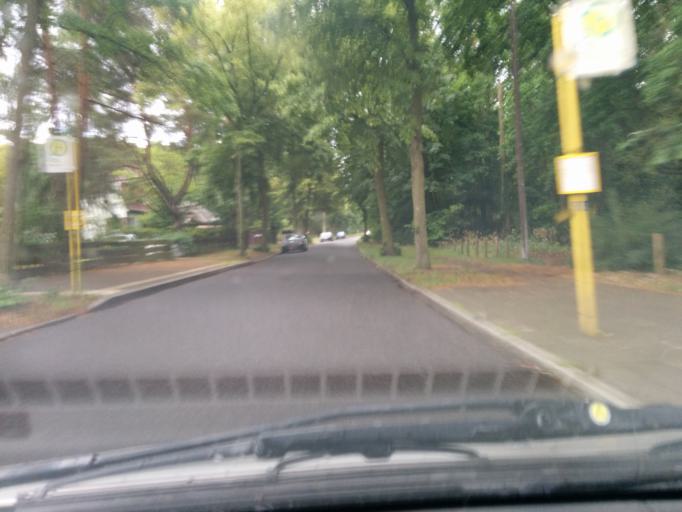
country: DE
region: Brandenburg
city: Falkensee
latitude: 52.5715
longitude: 13.1302
